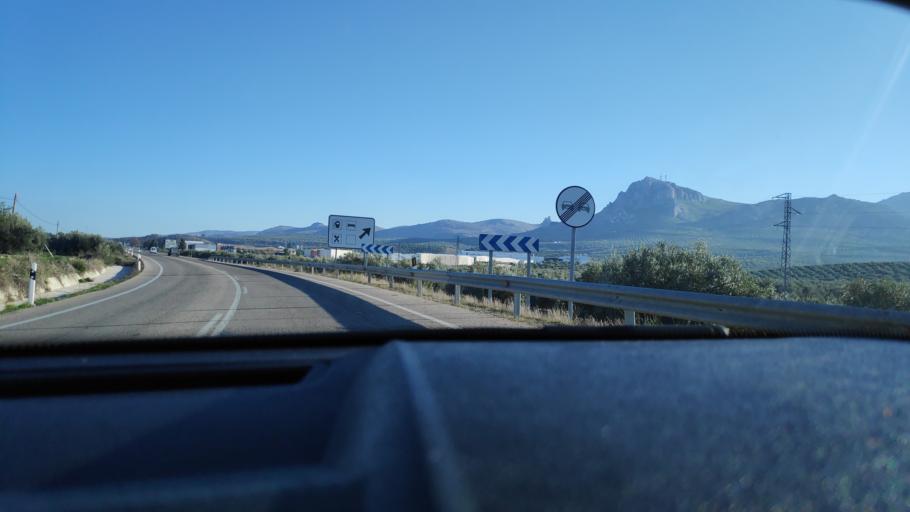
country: ES
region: Andalusia
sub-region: Province of Cordoba
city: Luque
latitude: 37.5842
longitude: -4.2898
